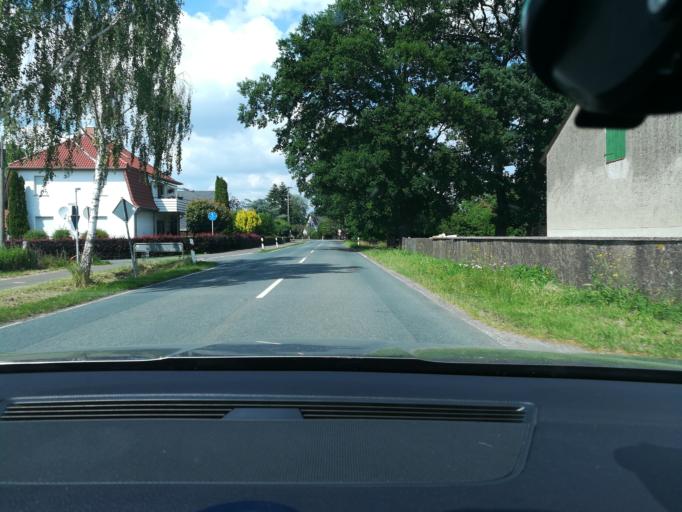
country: DE
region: North Rhine-Westphalia
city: Espelkamp
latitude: 52.3604
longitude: 8.6779
